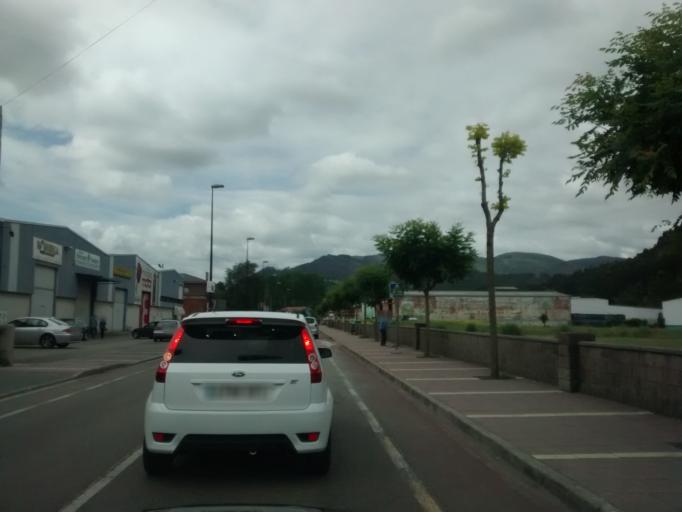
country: ES
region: Cantabria
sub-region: Provincia de Cantabria
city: Cartes
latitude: 43.3322
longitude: -4.0657
